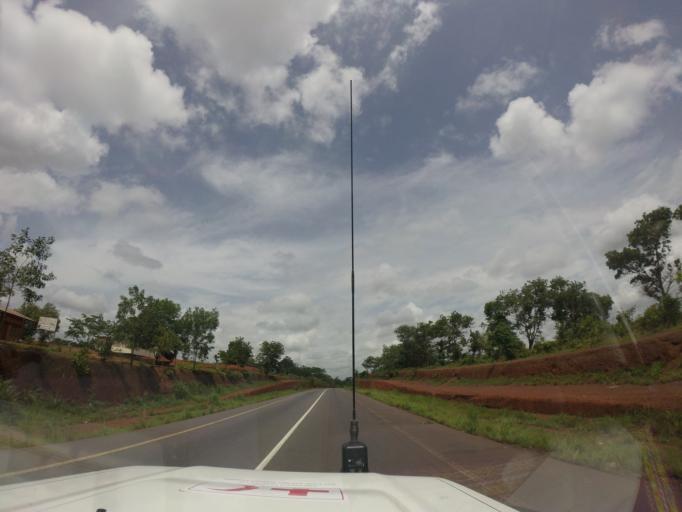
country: SL
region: Northern Province
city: Port Loko
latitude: 8.7718
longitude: -12.7745
